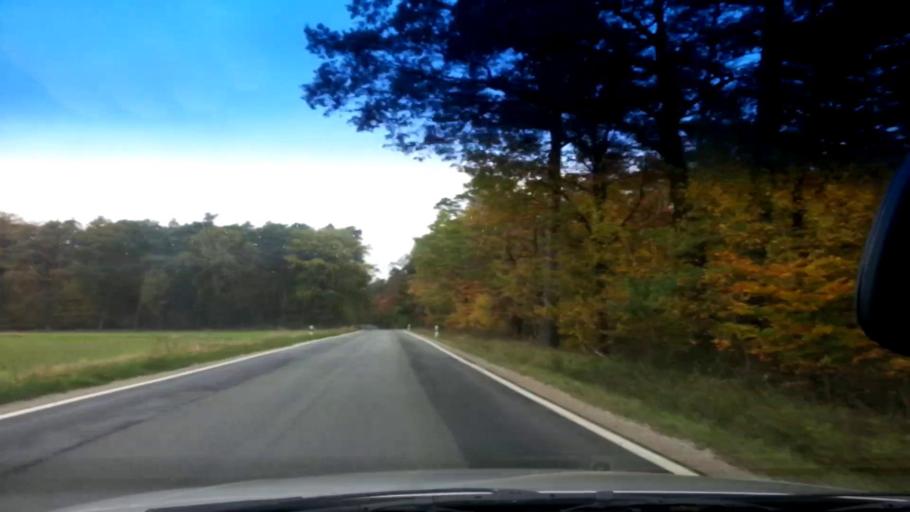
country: DE
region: Bavaria
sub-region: Upper Franconia
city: Burgebrach
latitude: 49.8103
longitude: 10.7842
